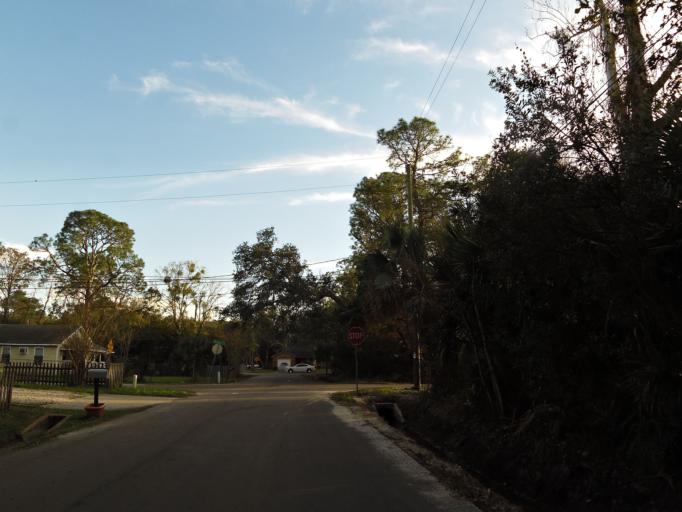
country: US
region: Florida
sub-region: Duval County
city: Jacksonville
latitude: 30.2891
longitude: -81.6423
